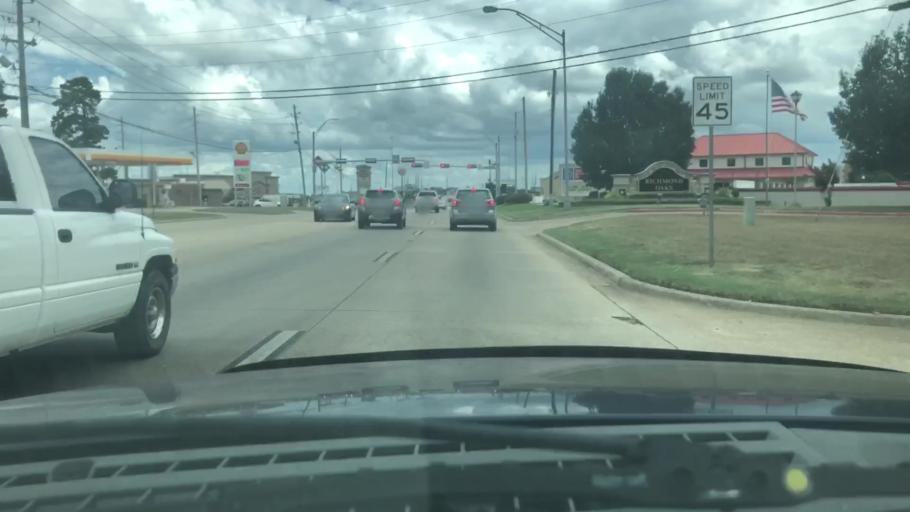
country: US
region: Texas
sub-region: Bowie County
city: Wake Village
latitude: 33.4613
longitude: -94.0916
